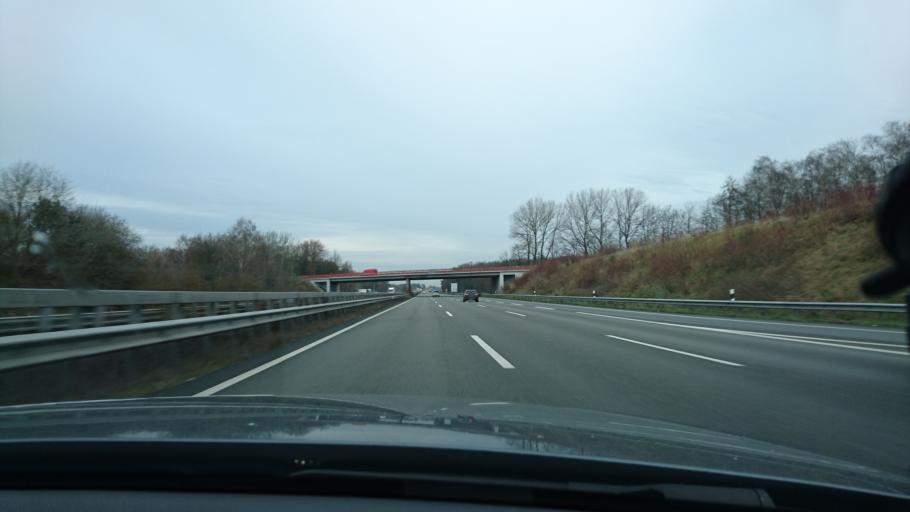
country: DE
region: Lower Saxony
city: Wallenhorst
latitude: 52.3930
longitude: 8.0392
